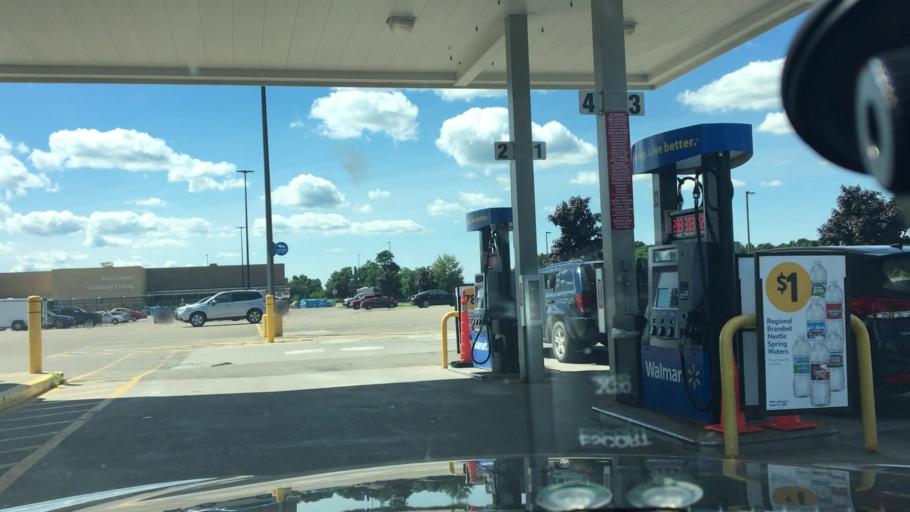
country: US
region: New York
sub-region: Erie County
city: Springville
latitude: 42.5014
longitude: -78.6906
